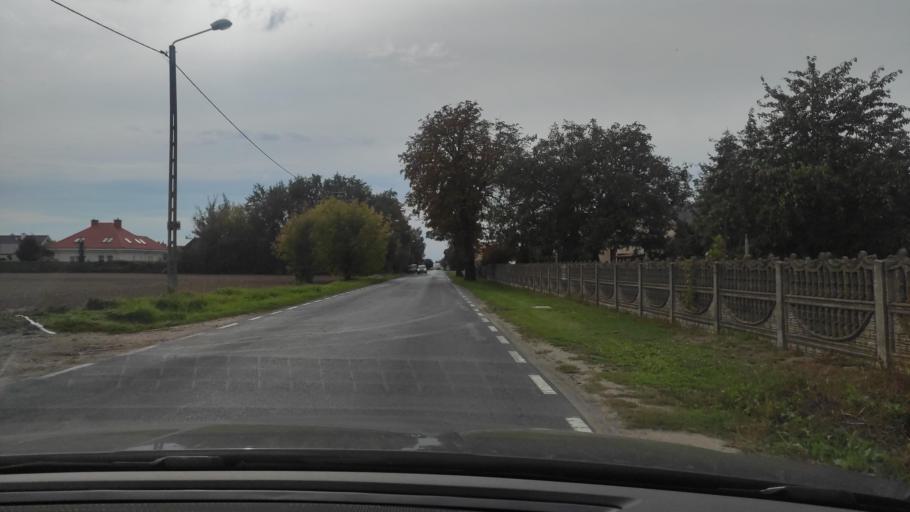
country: PL
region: Greater Poland Voivodeship
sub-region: Powiat poznanski
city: Kleszczewo
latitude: 52.3655
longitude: 17.1393
